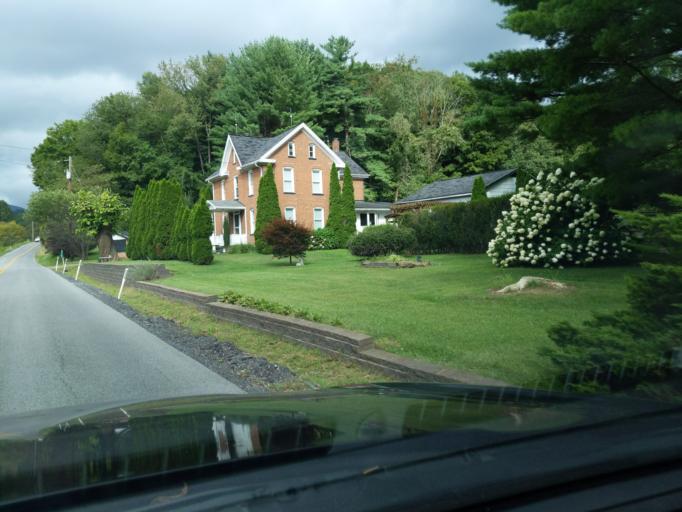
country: US
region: Pennsylvania
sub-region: Blair County
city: Claysburg
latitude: 40.3535
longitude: -78.4548
